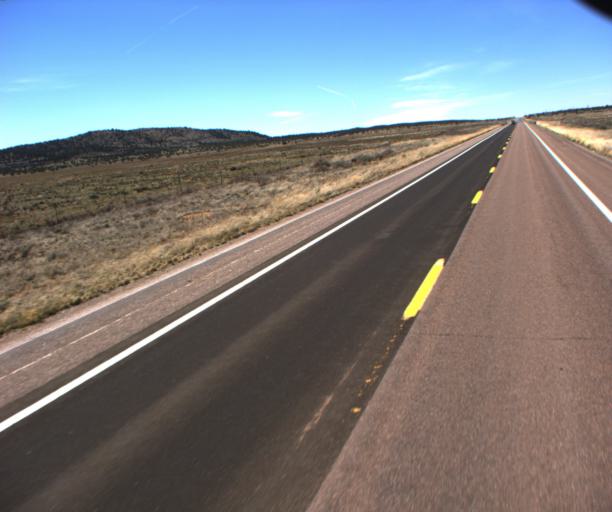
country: US
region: Arizona
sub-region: Mohave County
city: Peach Springs
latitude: 35.4855
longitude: -113.1488
